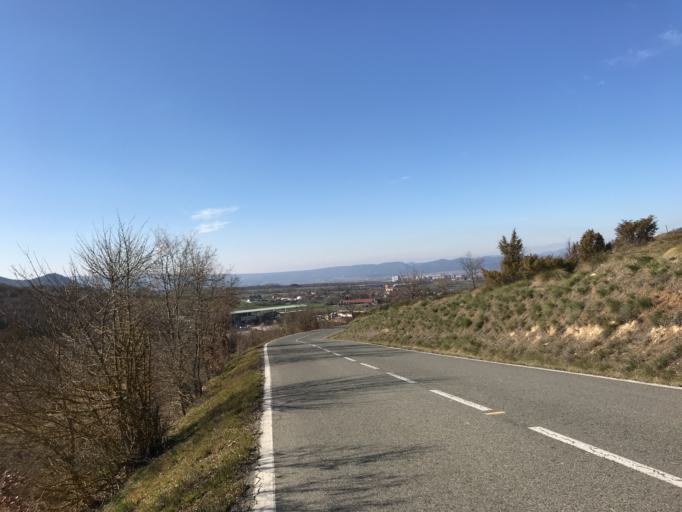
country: ES
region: Basque Country
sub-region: Provincia de Alava
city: Gasteiz / Vitoria
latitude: 42.8094
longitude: -2.6785
